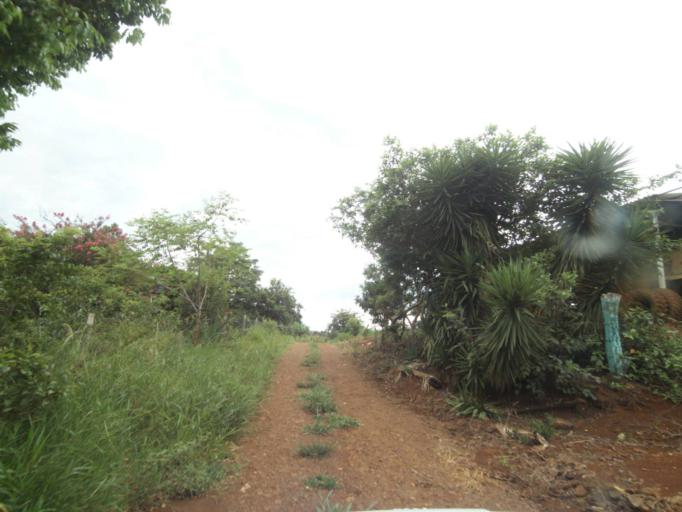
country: BR
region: Parana
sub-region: Guaraniacu
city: Guaraniacu
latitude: -24.9097
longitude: -52.9365
